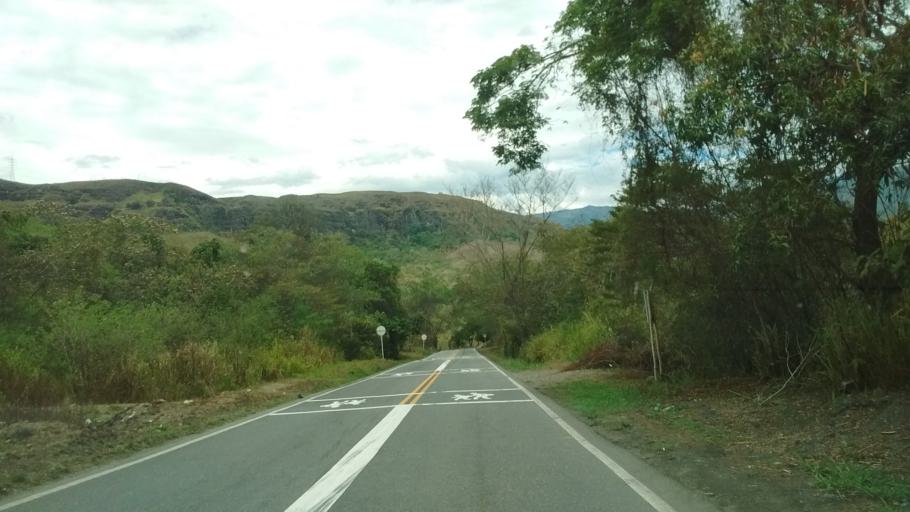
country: CO
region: Cauca
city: La Sierra
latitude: 2.2029
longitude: -76.8140
